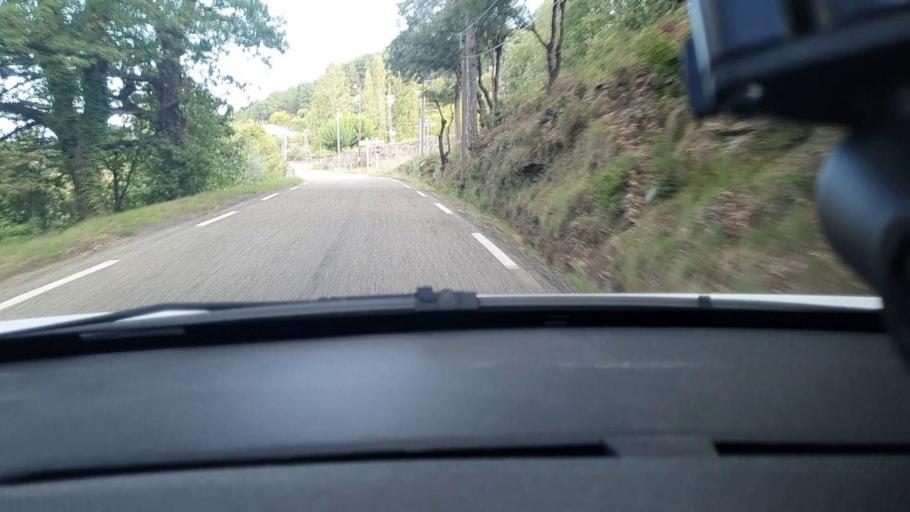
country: FR
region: Languedoc-Roussillon
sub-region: Departement du Gard
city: Besseges
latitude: 44.3143
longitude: 4.0748
